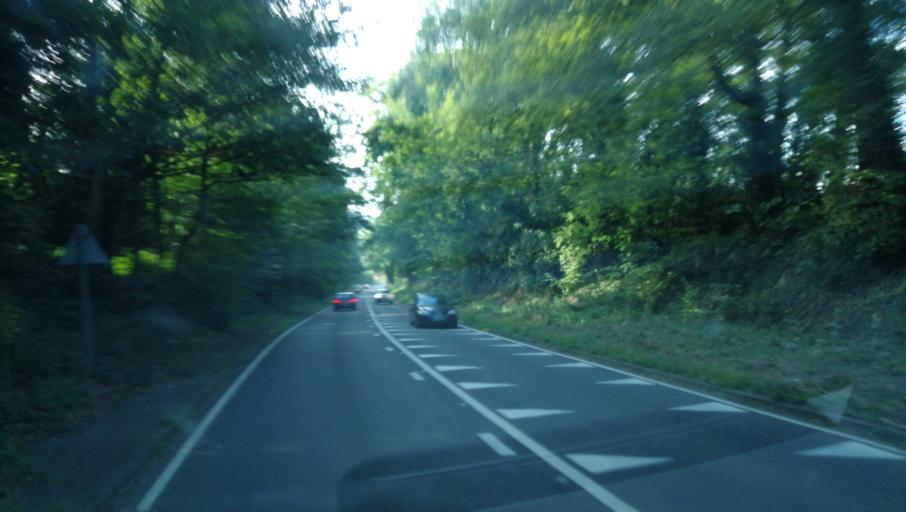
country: GB
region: England
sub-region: Oxfordshire
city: Deddington
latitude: 51.9767
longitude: -1.3190
